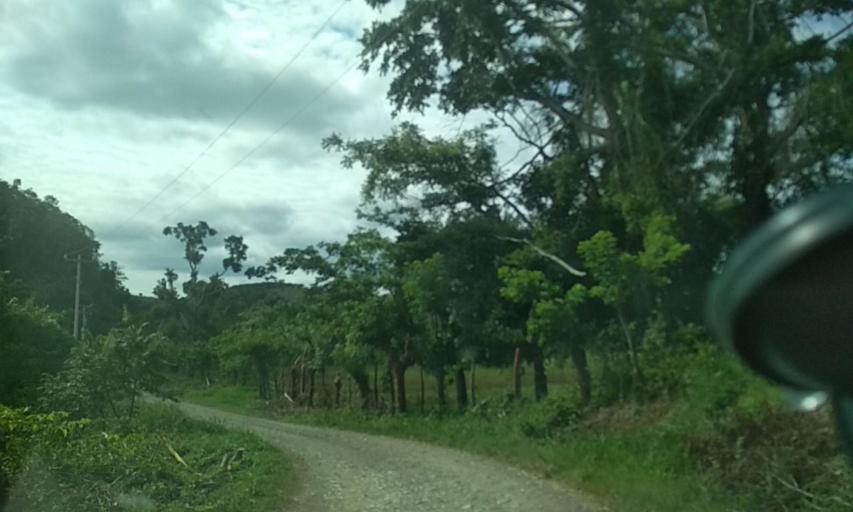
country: MX
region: Veracruz
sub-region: Papantla
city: Polutla
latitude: 20.5659
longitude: -97.1988
